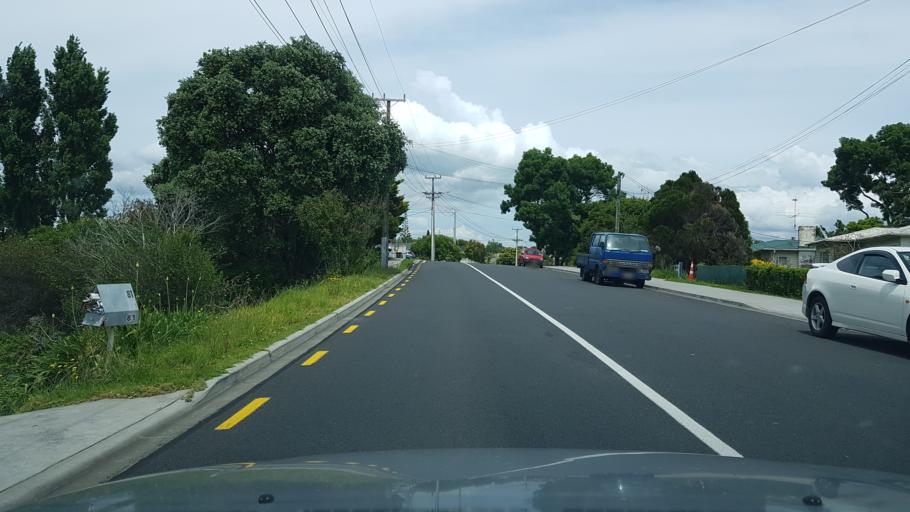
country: NZ
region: Auckland
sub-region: Auckland
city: North Shore
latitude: -36.7993
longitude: 174.7500
